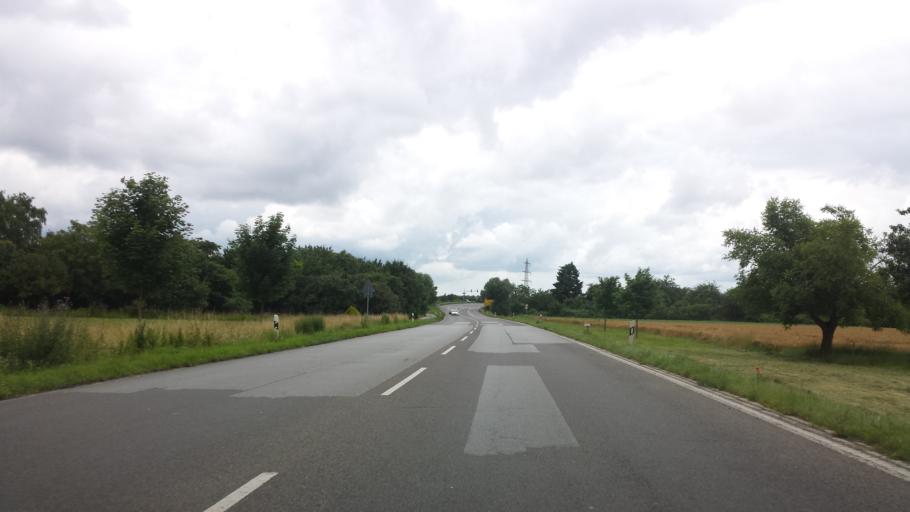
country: DE
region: Baden-Wuerttemberg
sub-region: Karlsruhe Region
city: Sandhausen
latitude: 49.3656
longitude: 8.6615
